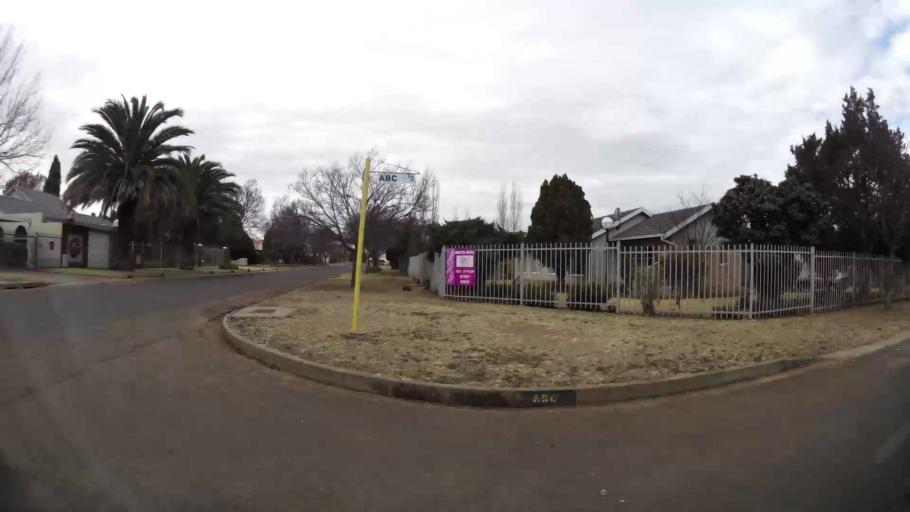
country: ZA
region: Orange Free State
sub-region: Fezile Dabi District Municipality
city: Kroonstad
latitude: -27.6358
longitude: 27.2398
